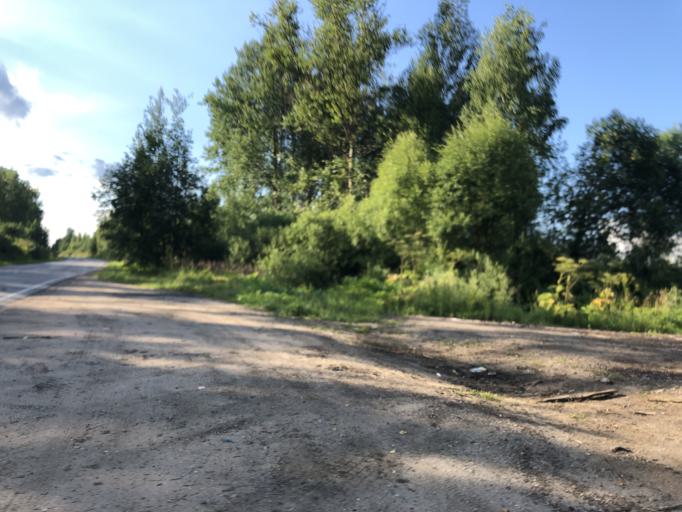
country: RU
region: Tverskaya
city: Rzhev
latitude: 56.2717
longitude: 34.2459
